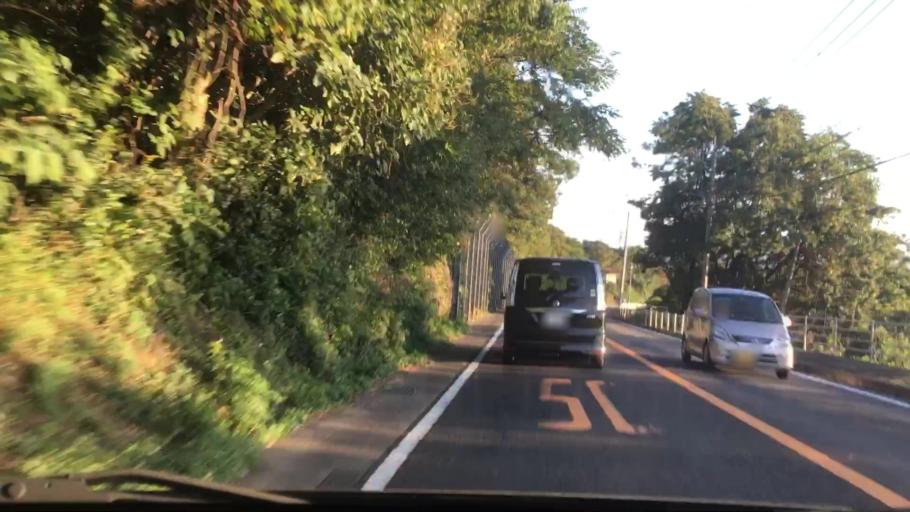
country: JP
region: Nagasaki
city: Sasebo
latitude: 33.0869
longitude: 129.7549
